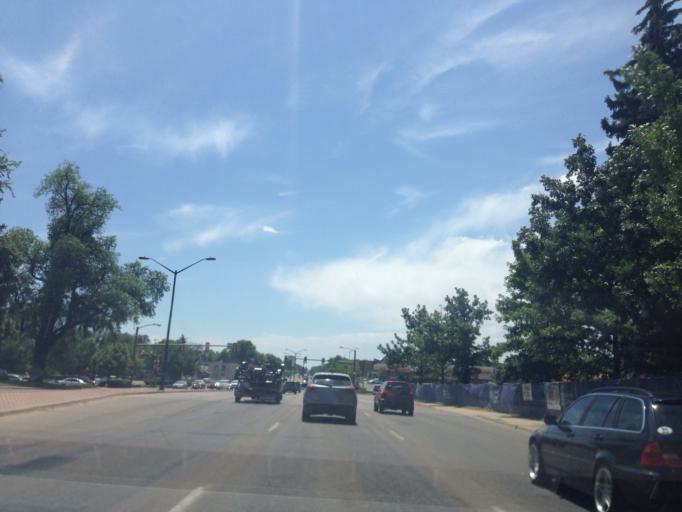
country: US
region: Colorado
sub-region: Larimer County
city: Fort Collins
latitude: 40.5682
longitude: -105.0770
